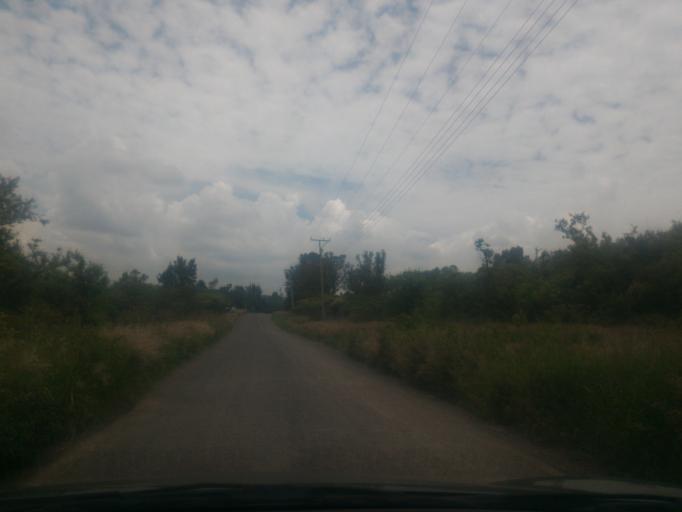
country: MX
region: Guanajuato
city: Ciudad Manuel Doblado
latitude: 20.8240
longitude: -102.0582
